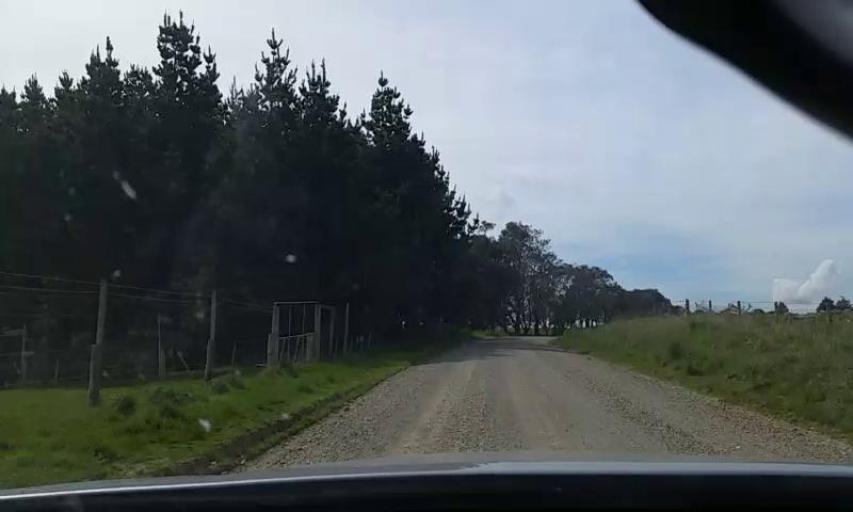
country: NZ
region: Otago
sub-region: Clutha District
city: Papatowai
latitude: -46.6328
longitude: 168.9748
